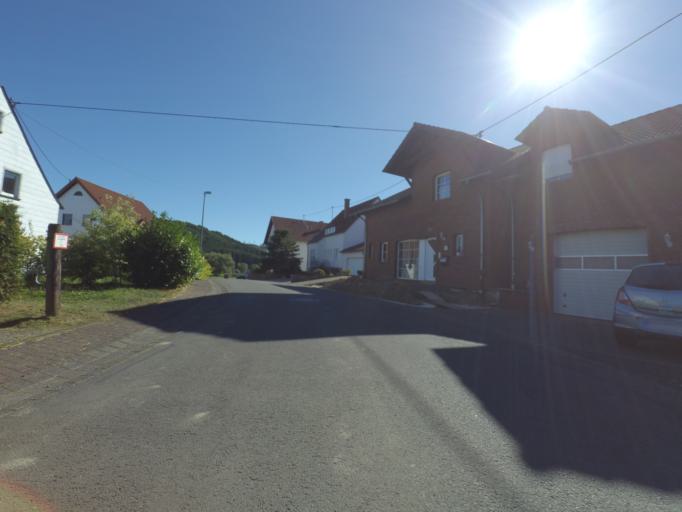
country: DE
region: Rheinland-Pfalz
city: Nerdlen
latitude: 50.2345
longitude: 6.8579
